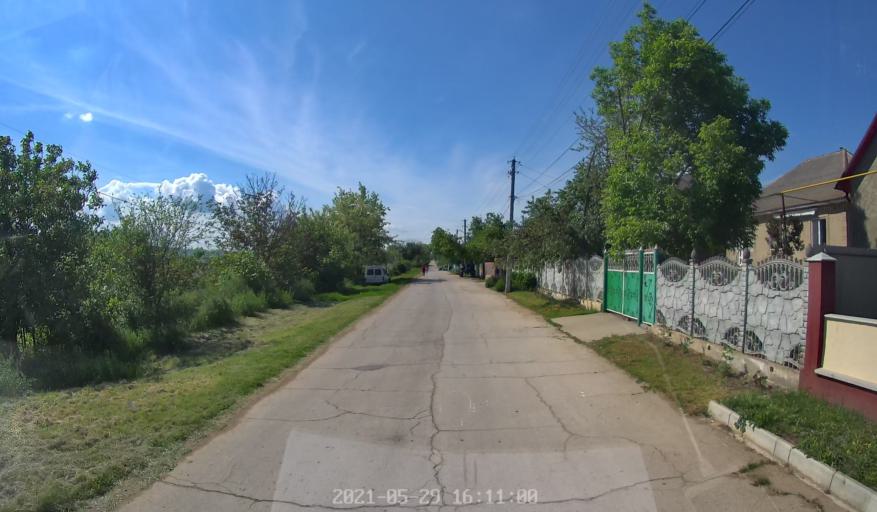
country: MD
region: Chisinau
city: Singera
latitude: 46.8244
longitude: 28.8790
